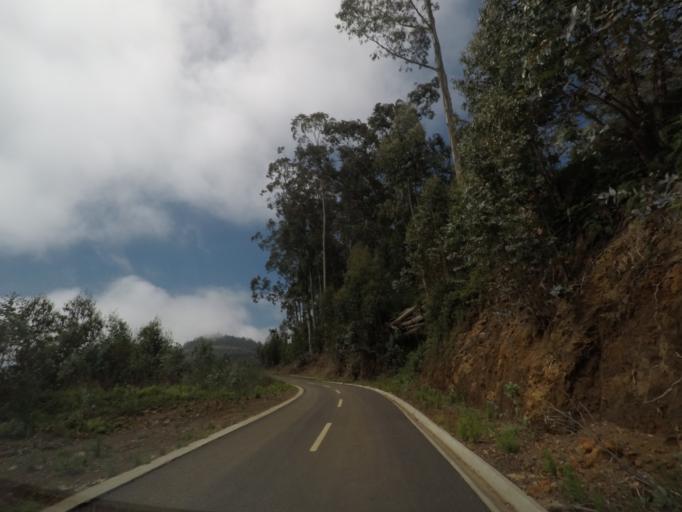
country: PT
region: Madeira
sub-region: Calheta
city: Arco da Calheta
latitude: 32.7244
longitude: -17.1217
